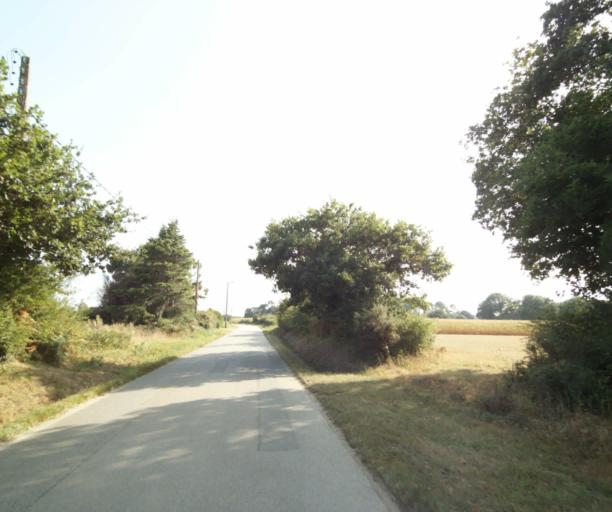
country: FR
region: Brittany
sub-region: Departement du Morbihan
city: Riantec
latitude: 47.7243
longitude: -3.2963
